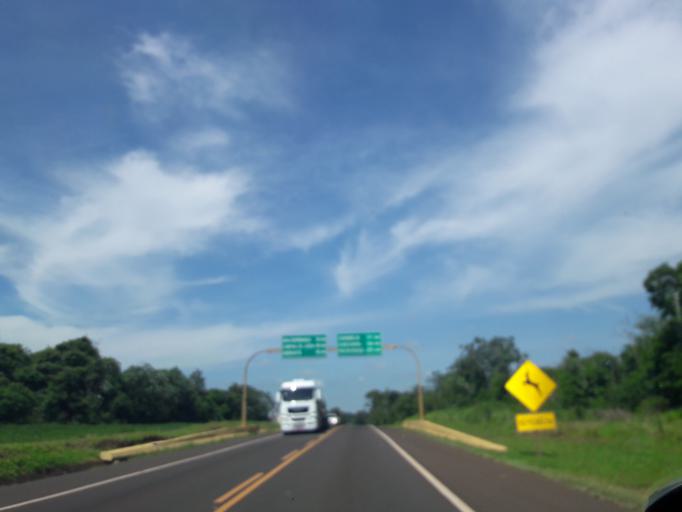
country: BR
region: Parana
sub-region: Campo Mourao
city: Campo Mourao
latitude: -24.2802
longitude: -52.5365
